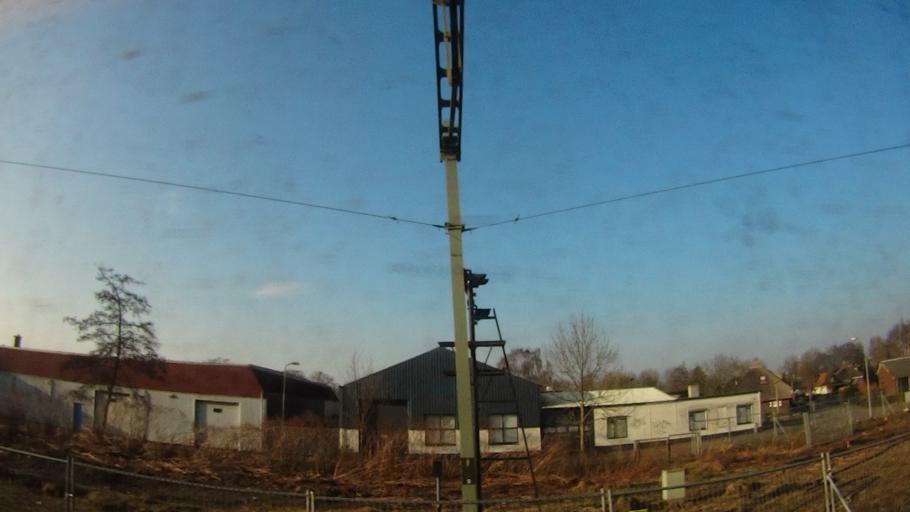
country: NL
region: Gelderland
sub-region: Gemeente Harderwijk
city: Harderwijk
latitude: 52.3366
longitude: 5.6150
